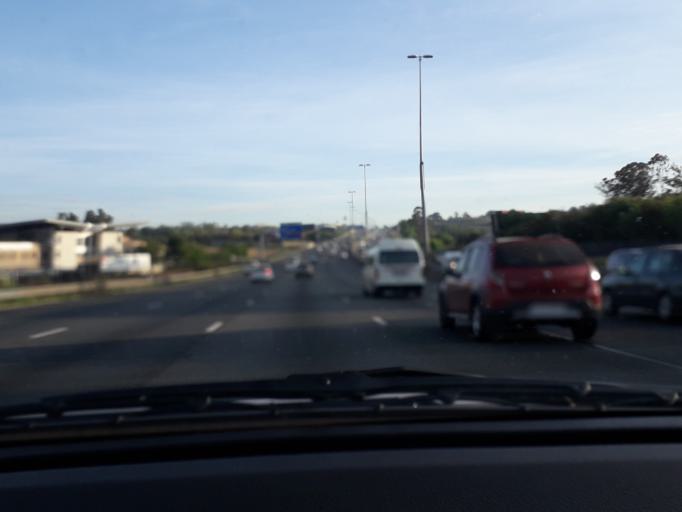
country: ZA
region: Gauteng
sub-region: City of Johannesburg Metropolitan Municipality
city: Midrand
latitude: -25.9965
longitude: 28.1214
